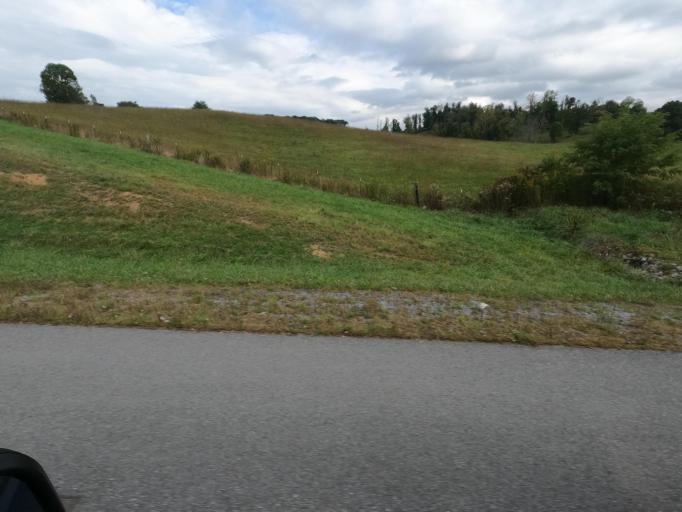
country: US
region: Tennessee
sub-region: Carter County
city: Central
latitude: 36.2997
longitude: -82.2465
